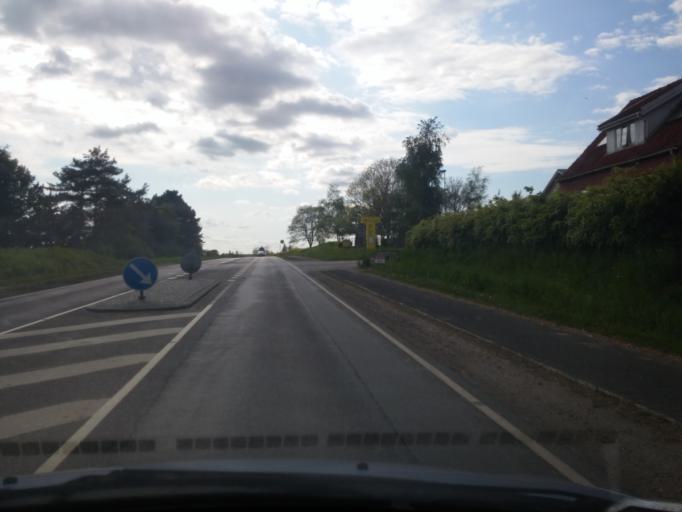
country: DK
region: South Denmark
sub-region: Nyborg Kommune
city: Ullerslev
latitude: 55.3645
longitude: 10.6598
